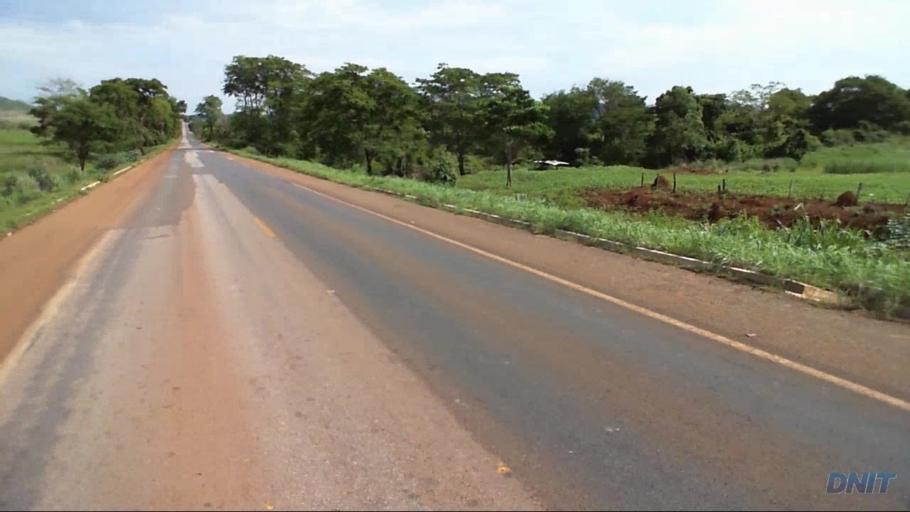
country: BR
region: Goias
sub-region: Barro Alto
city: Barro Alto
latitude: -15.0147
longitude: -48.8996
